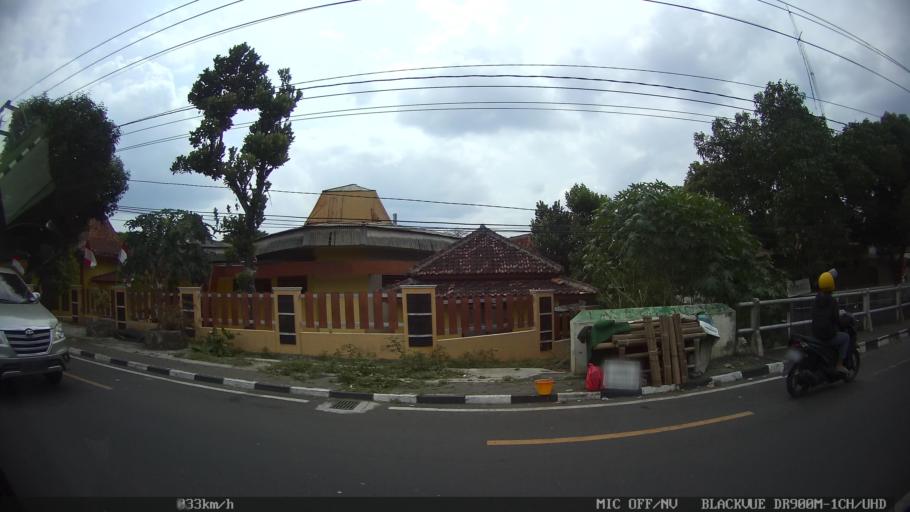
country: ID
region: Daerah Istimewa Yogyakarta
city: Yogyakarta
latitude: -7.7901
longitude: 110.3804
